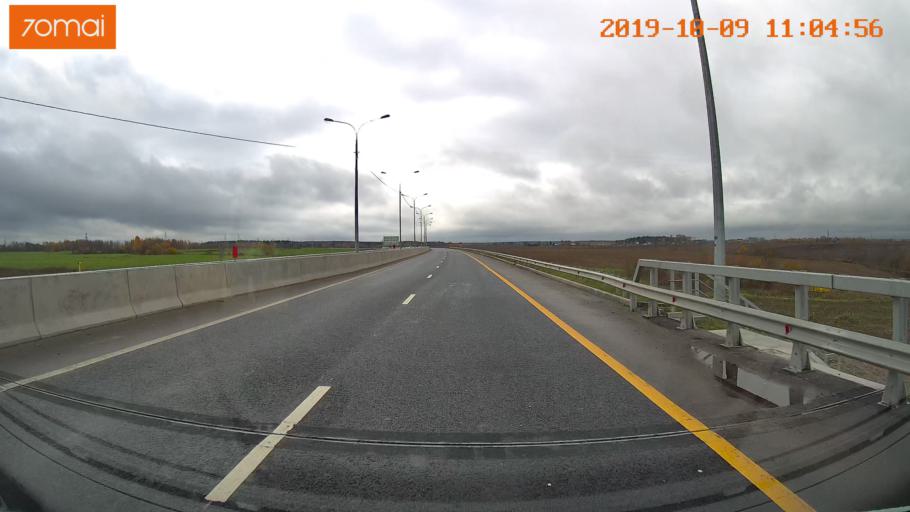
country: RU
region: Vologda
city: Molochnoye
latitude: 59.2063
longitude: 39.7619
